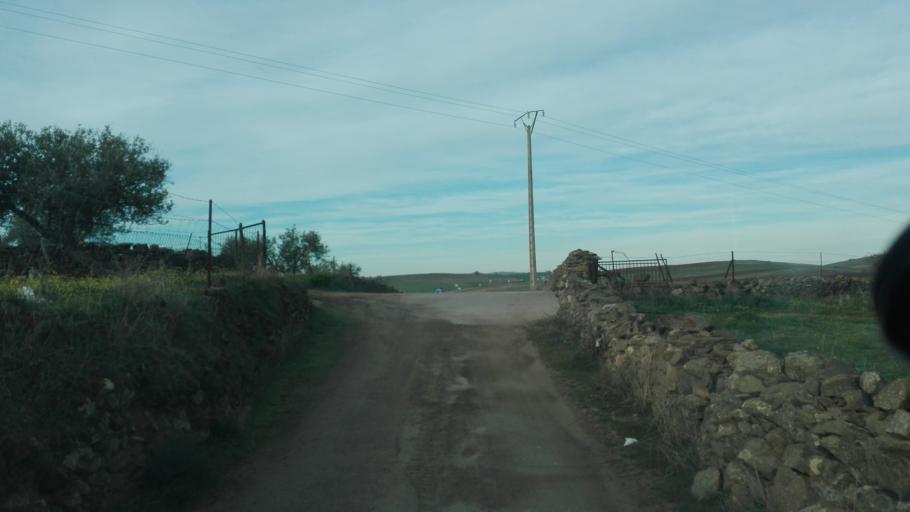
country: ES
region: Extremadura
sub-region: Provincia de Badajoz
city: Llera
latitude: 38.4497
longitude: -6.0598
